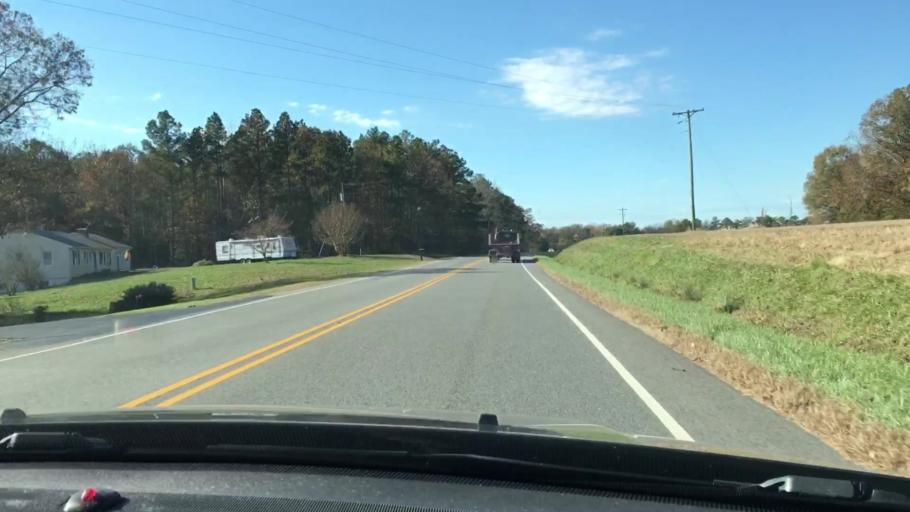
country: US
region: Virginia
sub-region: King William County
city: Central Garage
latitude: 37.7894
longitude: -77.1955
